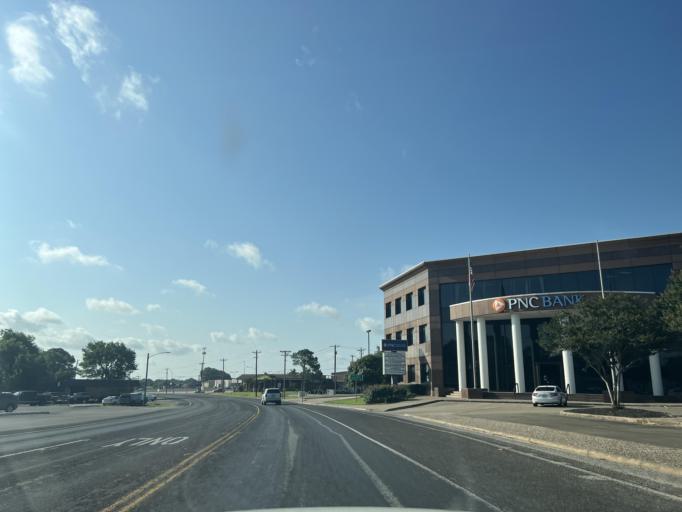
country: US
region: Texas
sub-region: Washington County
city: Brenham
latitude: 30.1517
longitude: -96.3914
